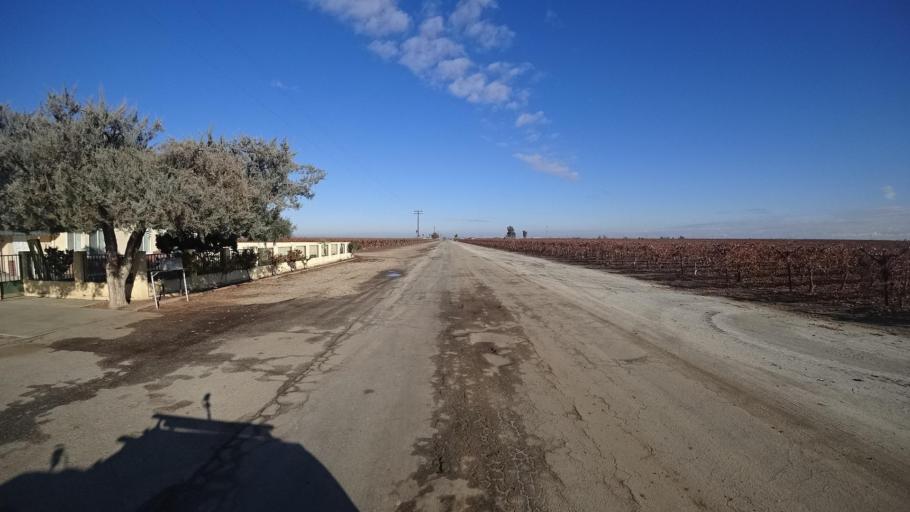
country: US
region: California
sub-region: Kern County
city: Delano
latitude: 35.7191
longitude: -119.2942
